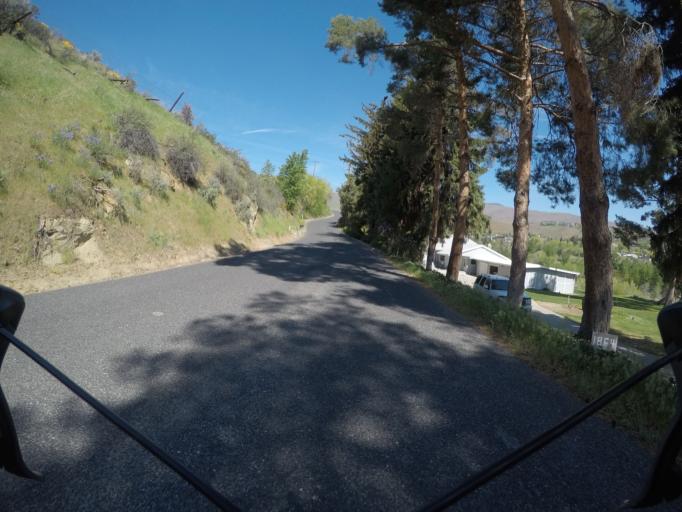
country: US
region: Washington
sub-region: Chelan County
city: West Wenatchee
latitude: 47.4749
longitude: -120.3819
